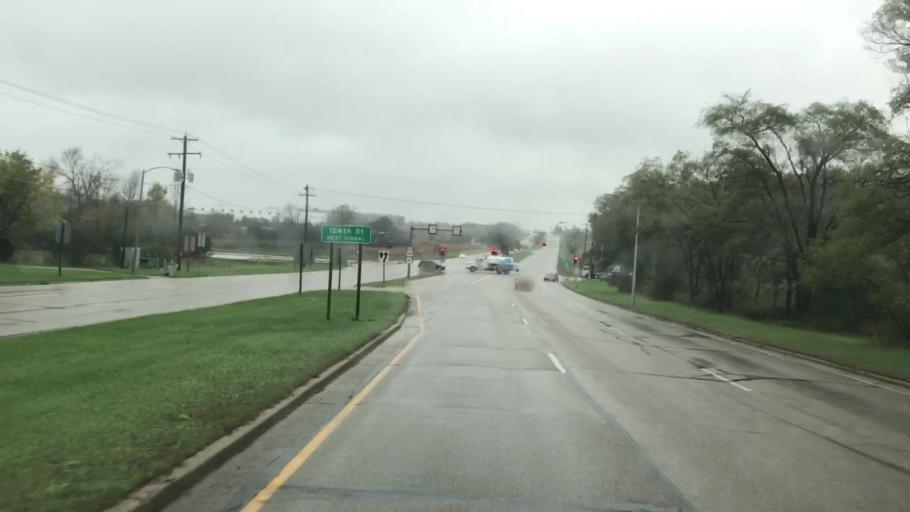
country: US
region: Wisconsin
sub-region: Waukesha County
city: Menomonee Falls
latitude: 43.1767
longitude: -88.0615
